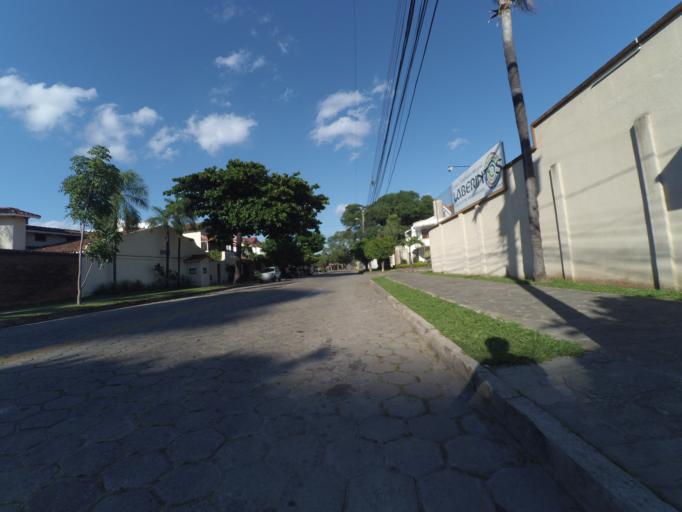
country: BO
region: Santa Cruz
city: Santa Cruz de la Sierra
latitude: -17.7993
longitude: -63.1968
